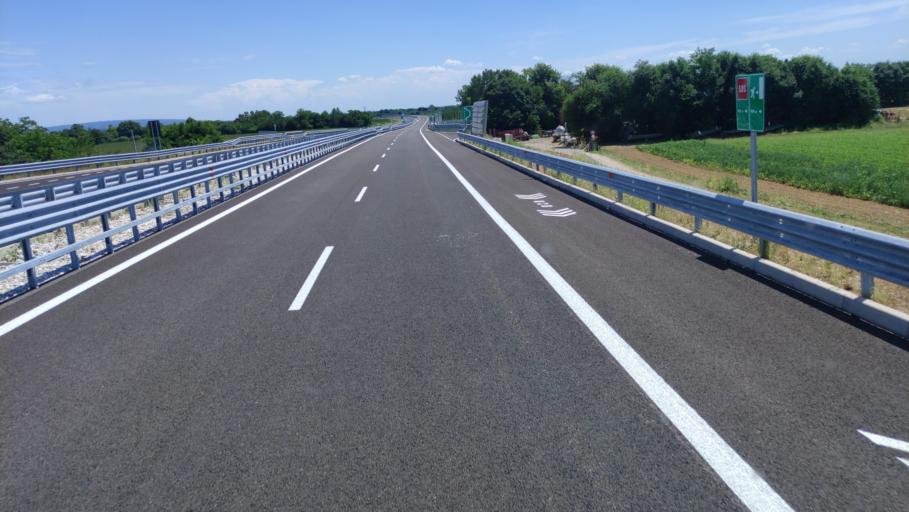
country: IT
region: Veneto
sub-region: Provincia di Treviso
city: Ca' Rainati
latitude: 45.7468
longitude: 11.8370
